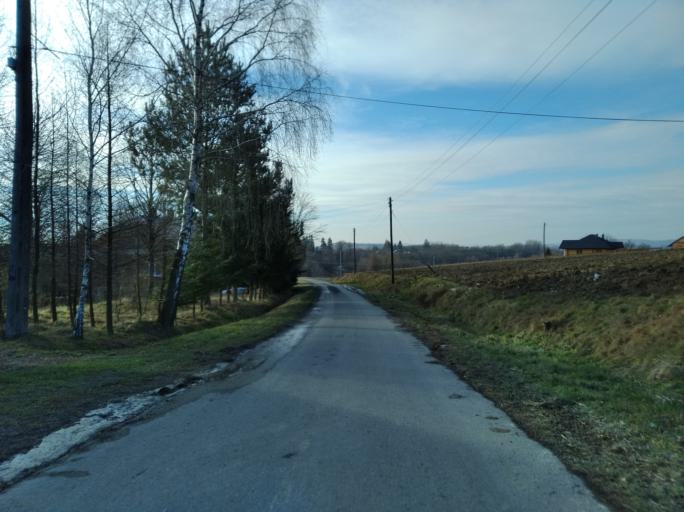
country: PL
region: Subcarpathian Voivodeship
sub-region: Powiat strzyzowski
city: Gwoznica Gorna
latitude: 49.8273
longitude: 21.9679
